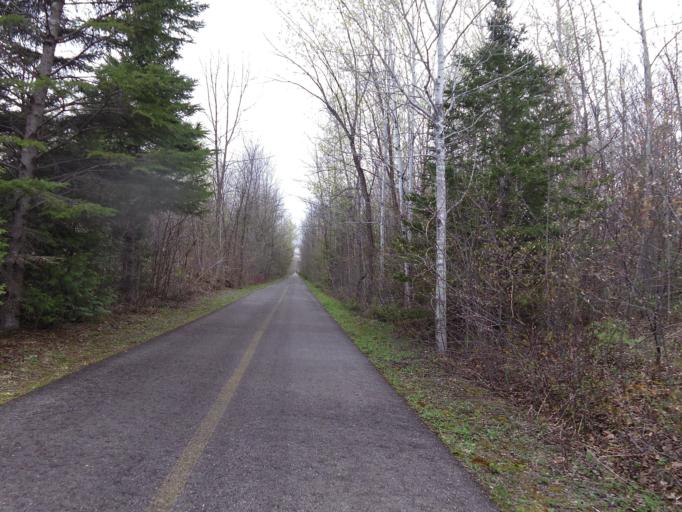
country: CA
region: Quebec
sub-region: Laurentides
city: Lachute
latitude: 45.5788
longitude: -74.3849
